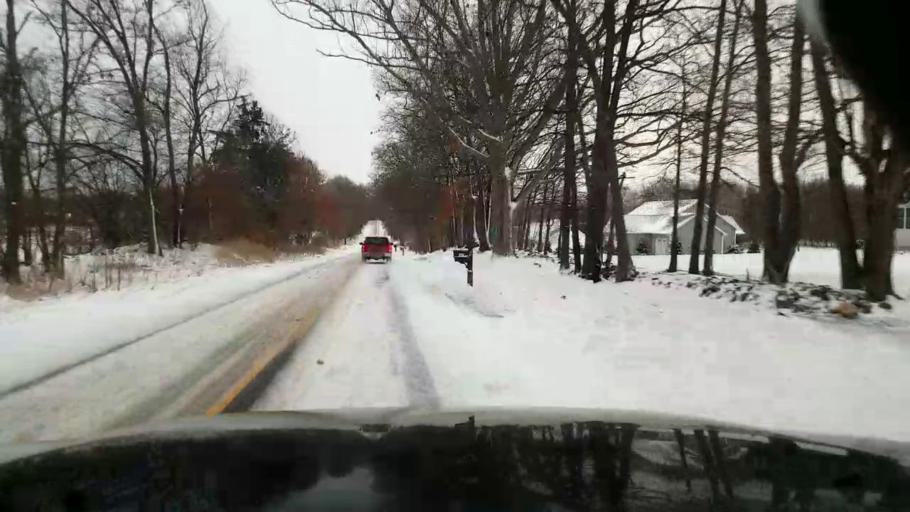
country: US
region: Michigan
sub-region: Jackson County
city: Spring Arbor
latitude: 42.1381
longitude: -84.4987
